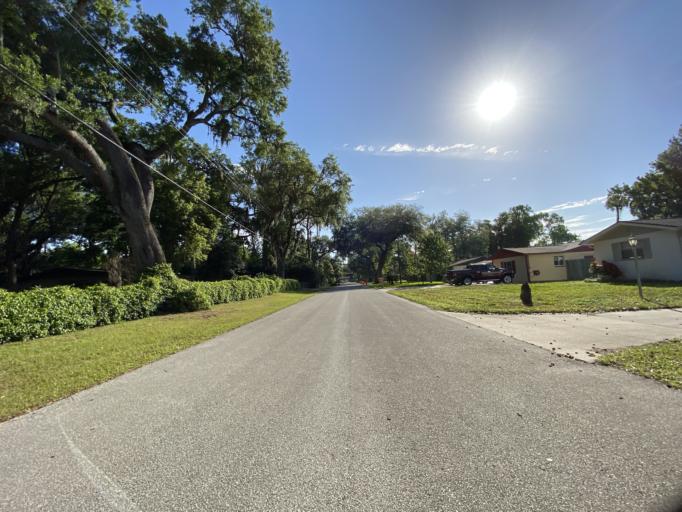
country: US
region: Florida
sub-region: Volusia County
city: South Daytona
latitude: 29.1772
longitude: -81.0188
